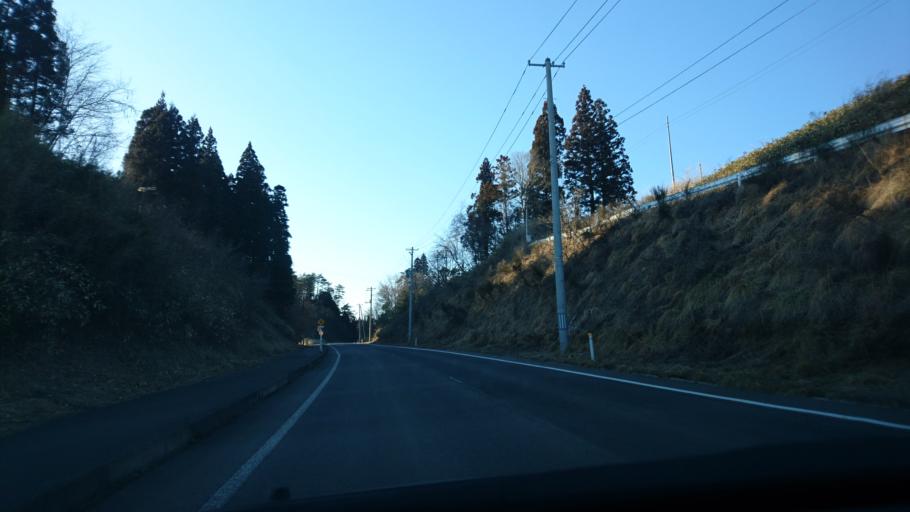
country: JP
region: Iwate
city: Ichinoseki
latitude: 38.9080
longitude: 141.3833
